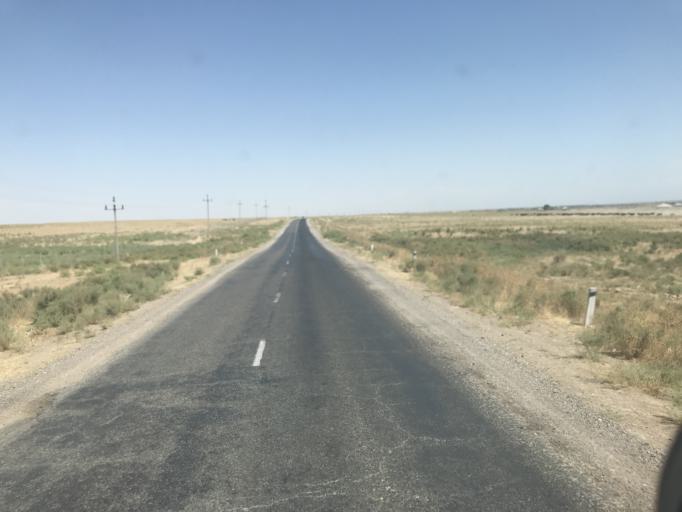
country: UZ
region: Toshkent
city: Amir Timur
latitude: 41.3577
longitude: 68.7208
